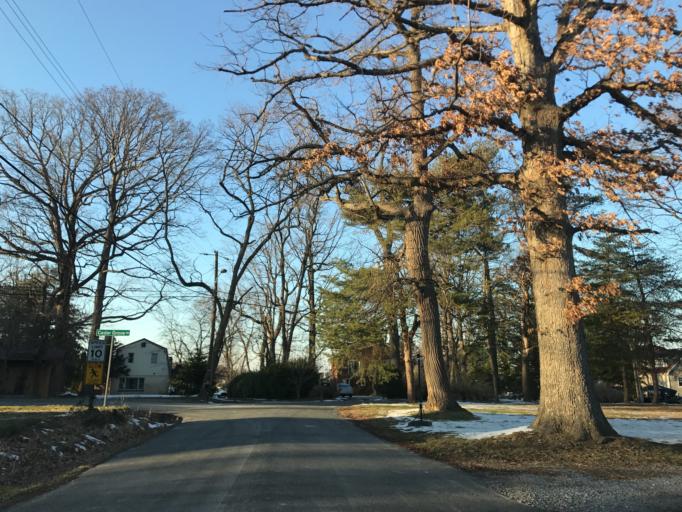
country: US
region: Maryland
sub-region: Baltimore County
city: Bowleys Quarters
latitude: 39.2840
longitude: -76.3987
